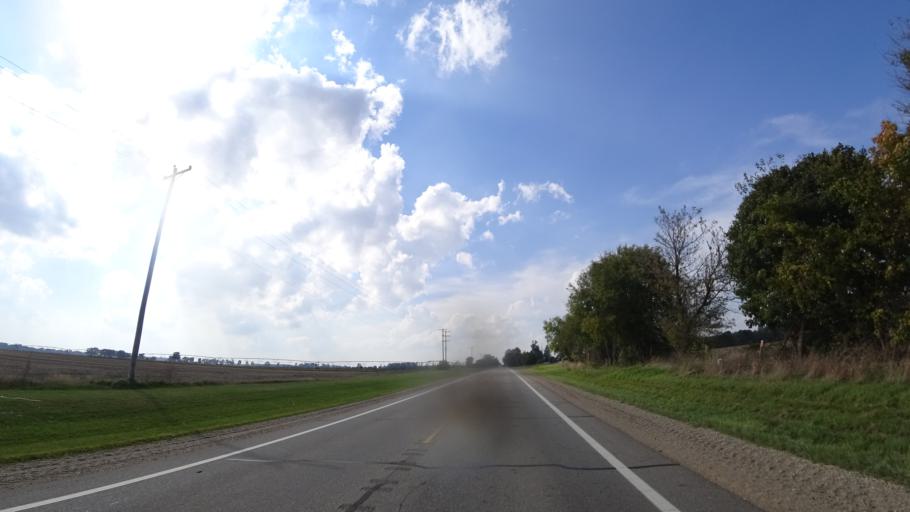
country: US
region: Michigan
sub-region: Saint Joseph County
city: Centreville
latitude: 42.0063
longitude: -85.4917
